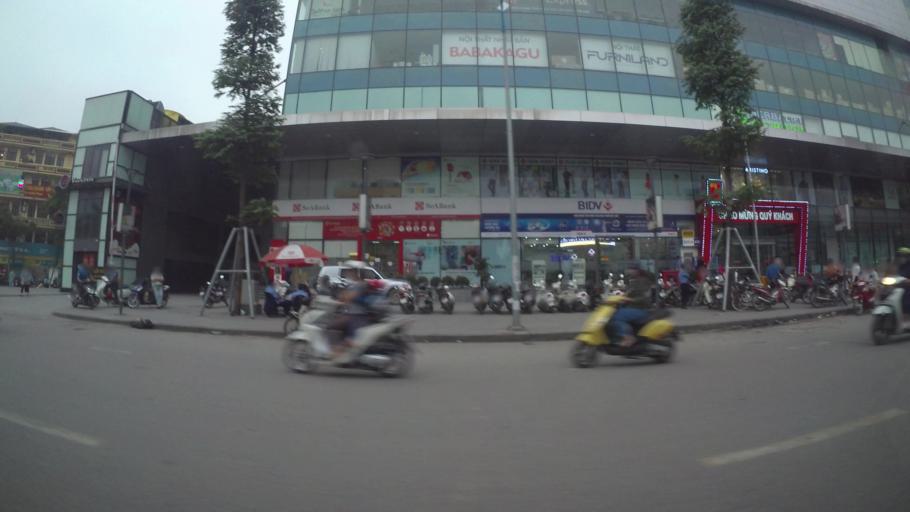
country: VN
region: Ha Noi
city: Dong Da
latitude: 20.9993
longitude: 105.8287
